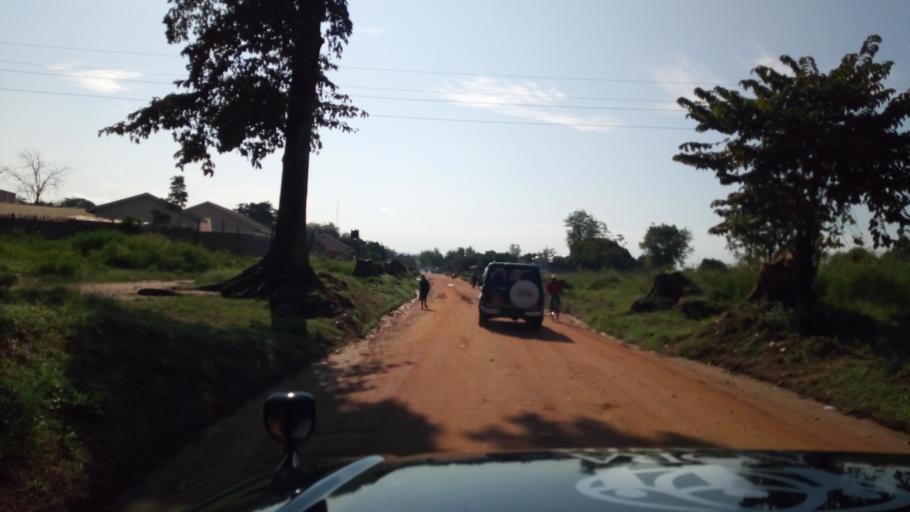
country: UG
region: Northern Region
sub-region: Adjumani District
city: Adjumani
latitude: 3.3765
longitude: 31.7936
